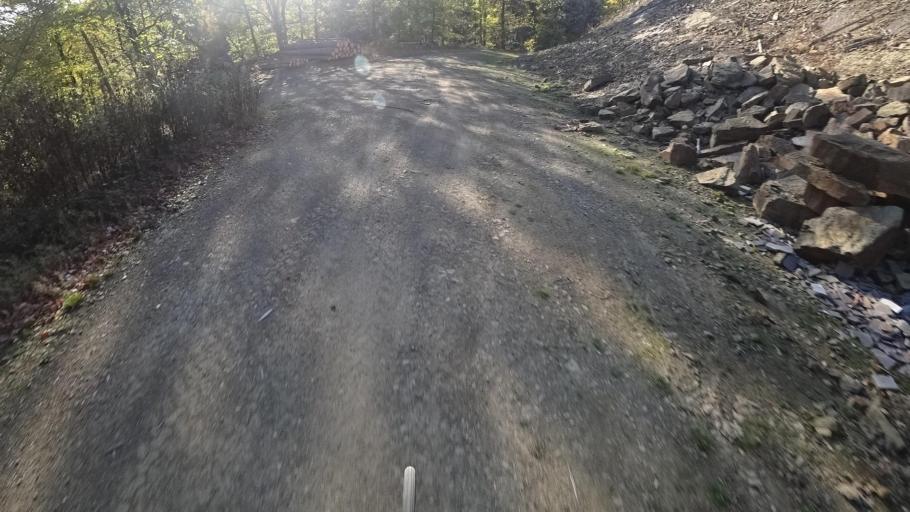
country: DE
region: Rheinland-Pfalz
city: Lind
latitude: 50.5217
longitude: 6.9453
